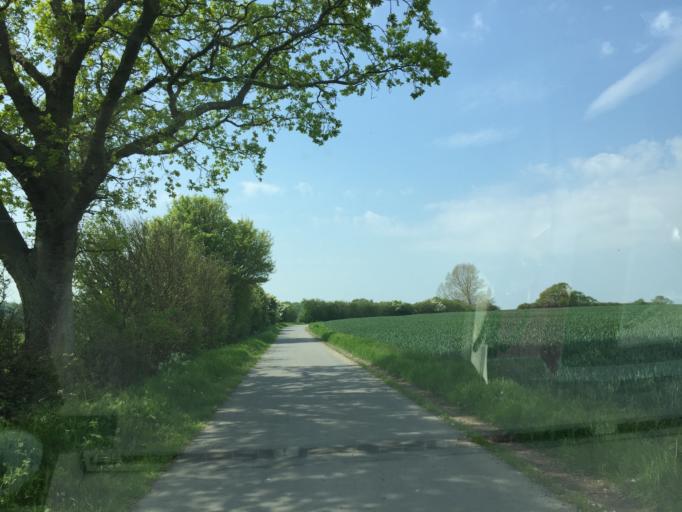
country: DK
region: South Denmark
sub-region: Langeland Kommune
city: Rudkobing
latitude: 54.9889
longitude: 10.8174
